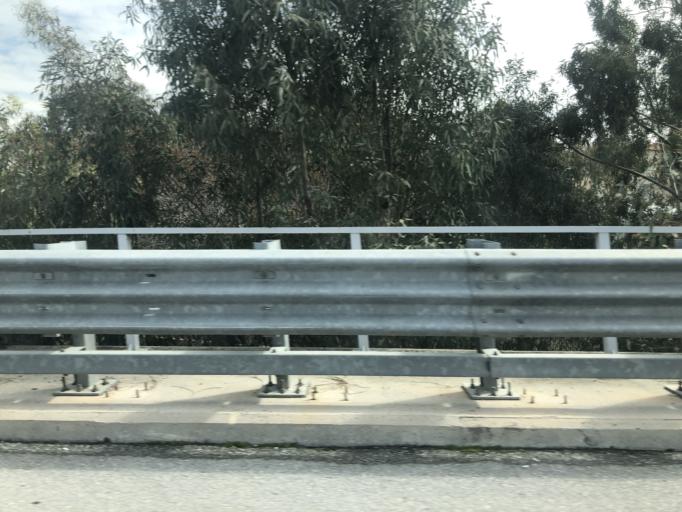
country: TR
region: Izmir
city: Karabaglar
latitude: 38.3976
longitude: 27.0635
